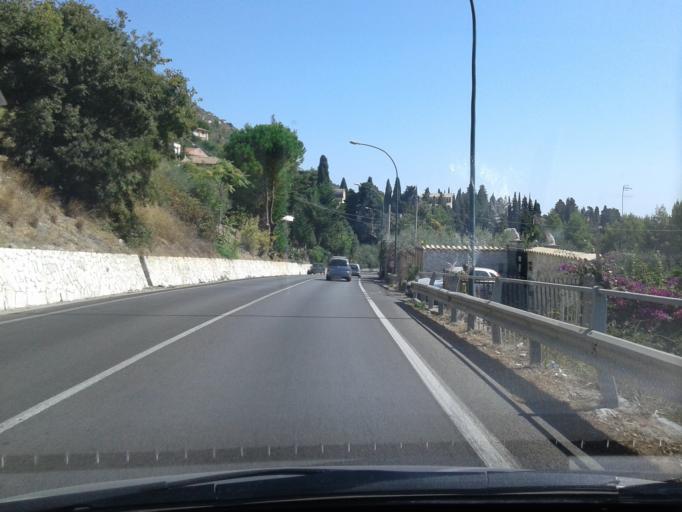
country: IT
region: Sicily
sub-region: Palermo
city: Cannizzaro-Favara
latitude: 38.0706
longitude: 13.2696
